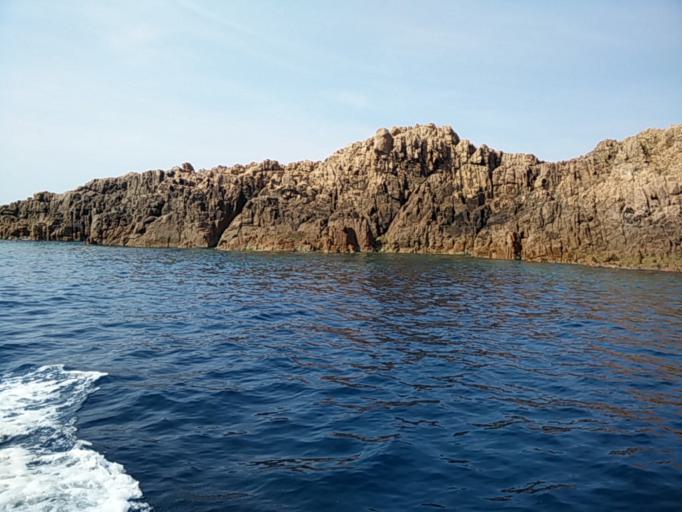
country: FR
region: Corsica
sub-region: Departement de la Corse-du-Sud
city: Cargese
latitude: 42.2361
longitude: 8.5395
